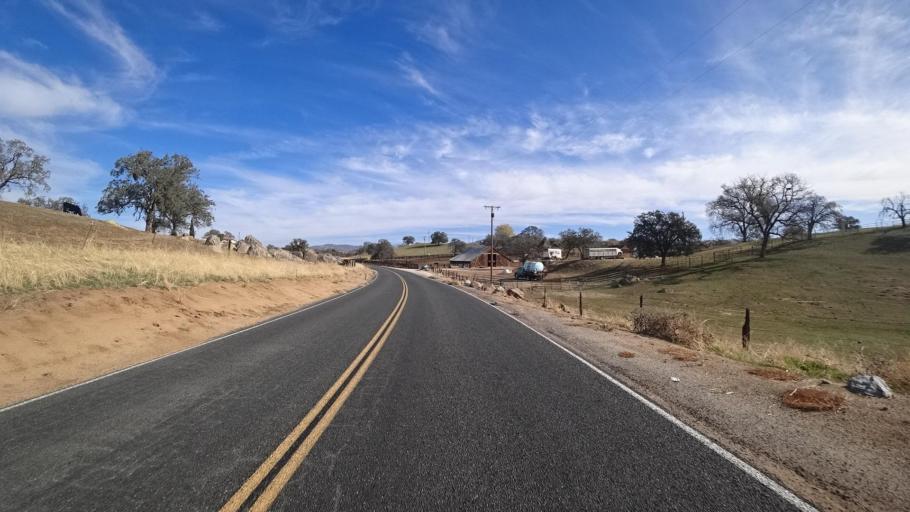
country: US
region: California
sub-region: Kern County
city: Oildale
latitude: 35.6181
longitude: -118.8508
